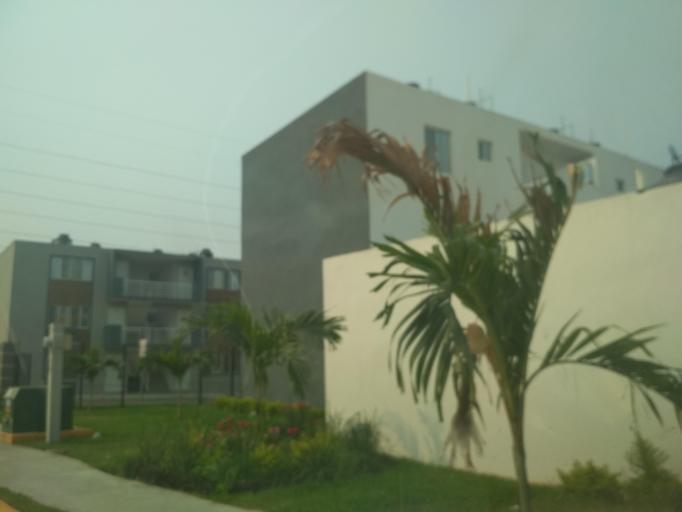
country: MX
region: Veracruz
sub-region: Veracruz
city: Las Amapolas
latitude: 19.1517
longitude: -96.2324
